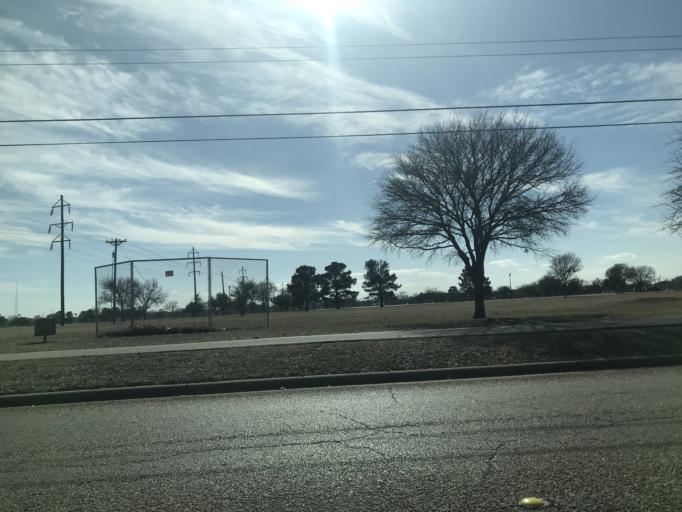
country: US
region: Texas
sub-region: Taylor County
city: Abilene
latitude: 32.4120
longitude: -99.7619
